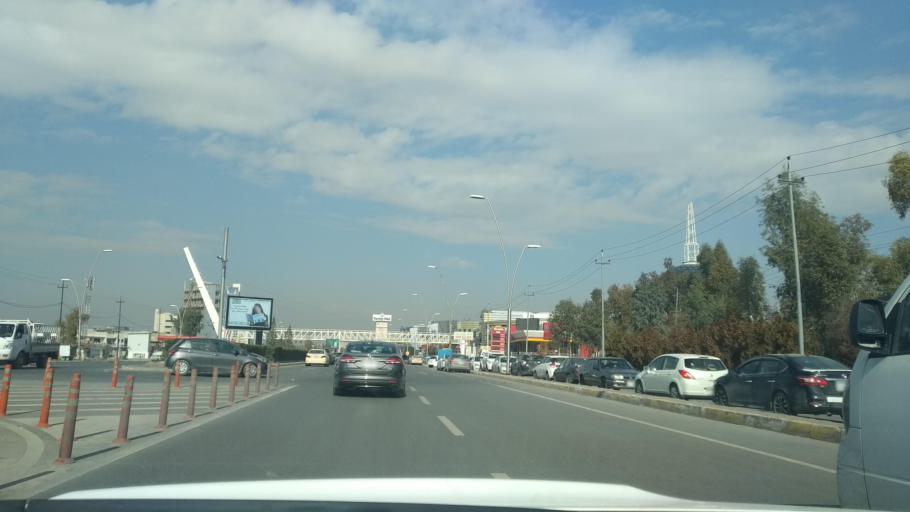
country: IQ
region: Arbil
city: Erbil
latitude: 36.2073
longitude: 44.0447
